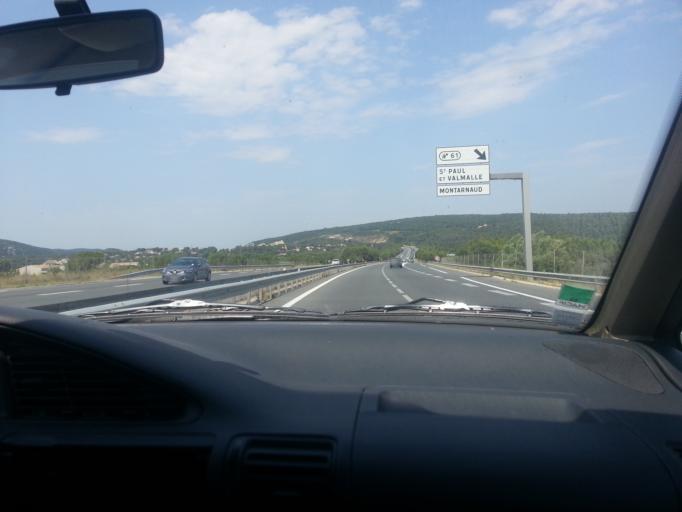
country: FR
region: Languedoc-Roussillon
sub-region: Departement de l'Herault
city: Montarnaud
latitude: 43.6283
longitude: 3.6988
